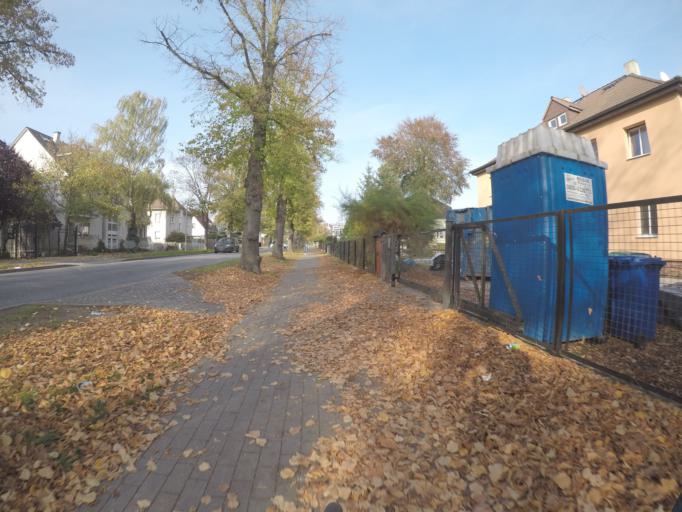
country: DE
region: Berlin
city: Buckow
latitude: 52.4097
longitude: 13.4401
